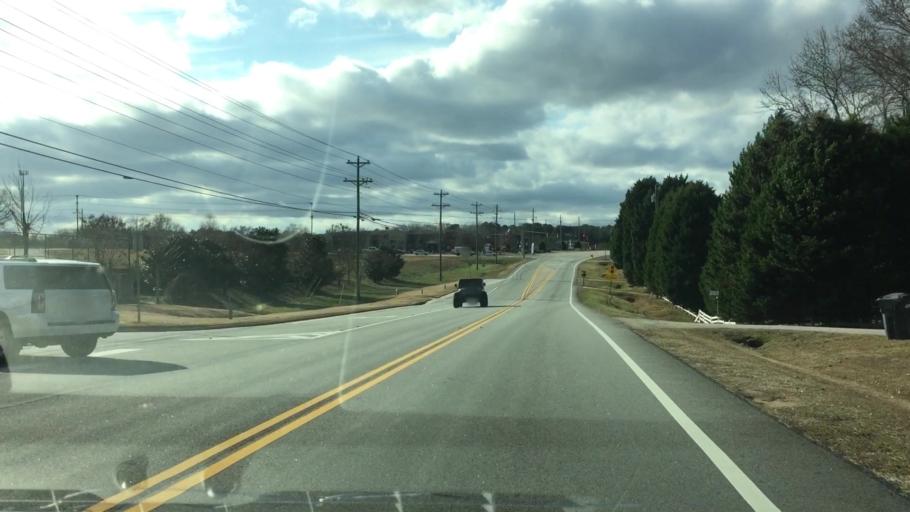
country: US
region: Georgia
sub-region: Henry County
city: McDonough
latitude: 33.4287
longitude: -84.0950
